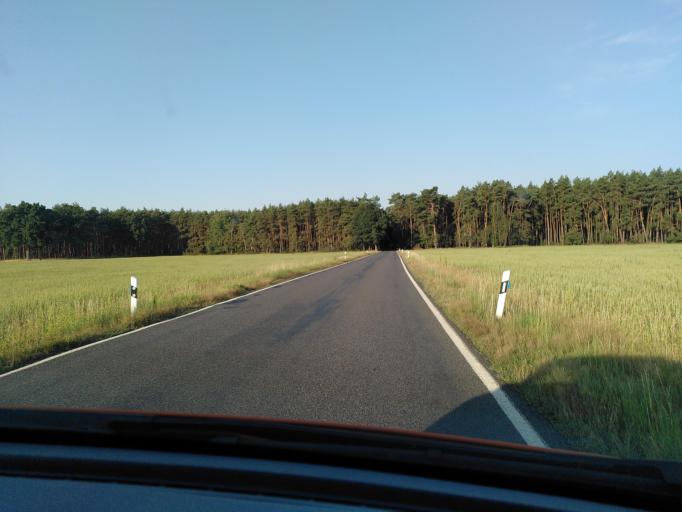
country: DE
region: Saxony
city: Horka
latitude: 51.2984
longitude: 14.2785
